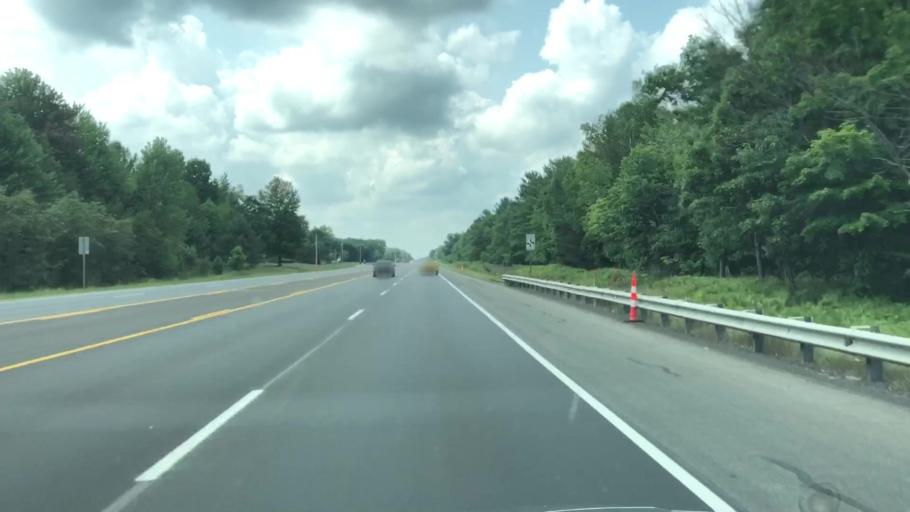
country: US
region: Michigan
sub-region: Isabella County
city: Shepherd
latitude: 43.6114
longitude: -84.5973
